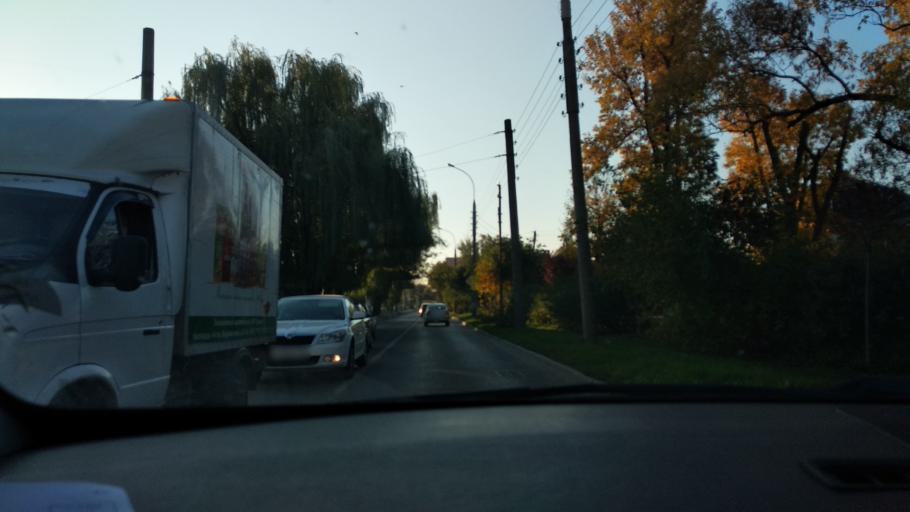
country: RU
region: Krasnodarskiy
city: Krasnodar
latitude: 45.0111
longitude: 39.0123
